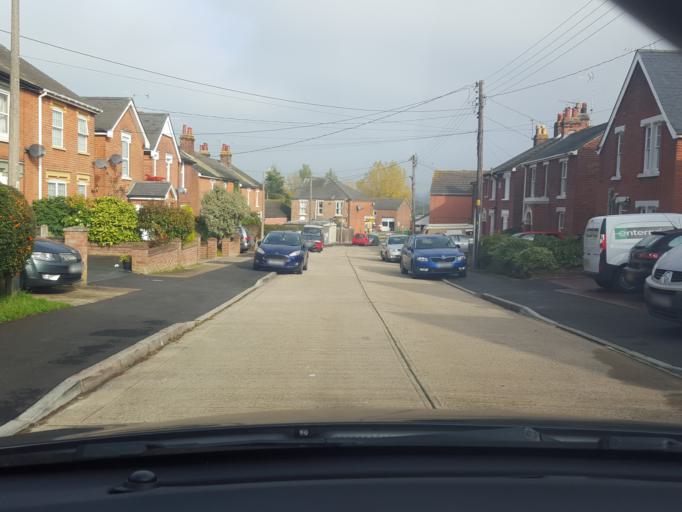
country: GB
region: England
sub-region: Essex
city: Manningtree
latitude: 51.9450
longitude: 1.0591
